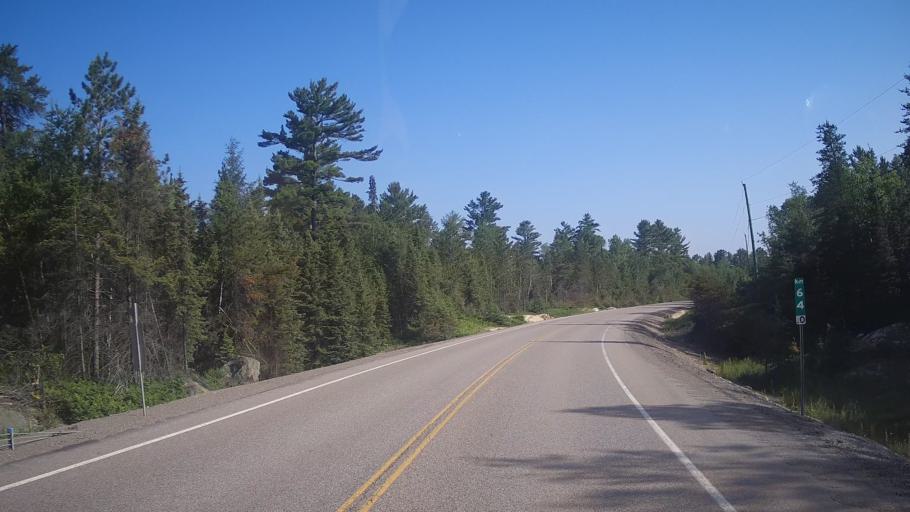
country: CA
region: Ontario
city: Rayside-Balfour
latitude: 46.7461
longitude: -81.6013
